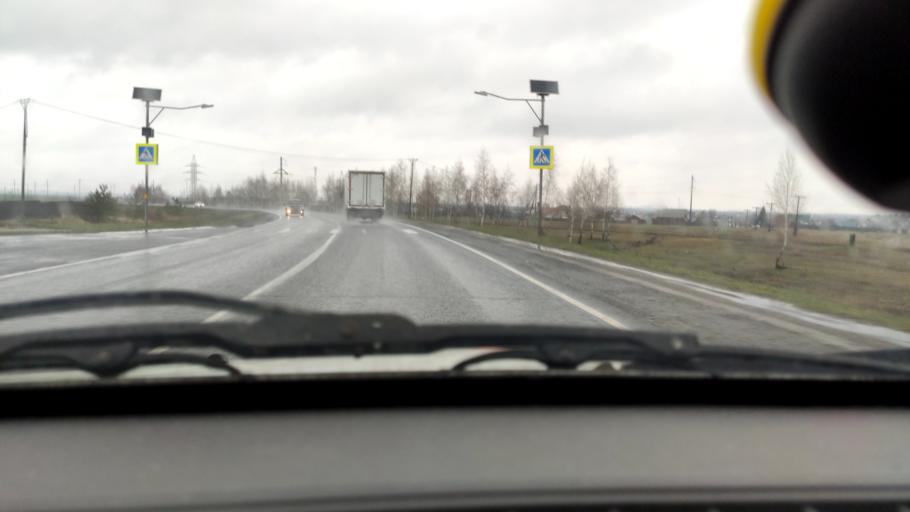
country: RU
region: Samara
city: Povolzhskiy
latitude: 53.6303
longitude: 49.6587
